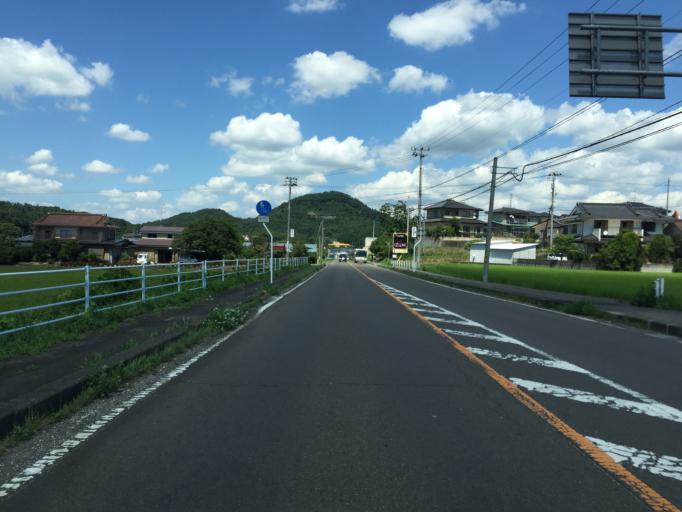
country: JP
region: Fukushima
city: Nihommatsu
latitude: 37.6292
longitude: 140.4611
